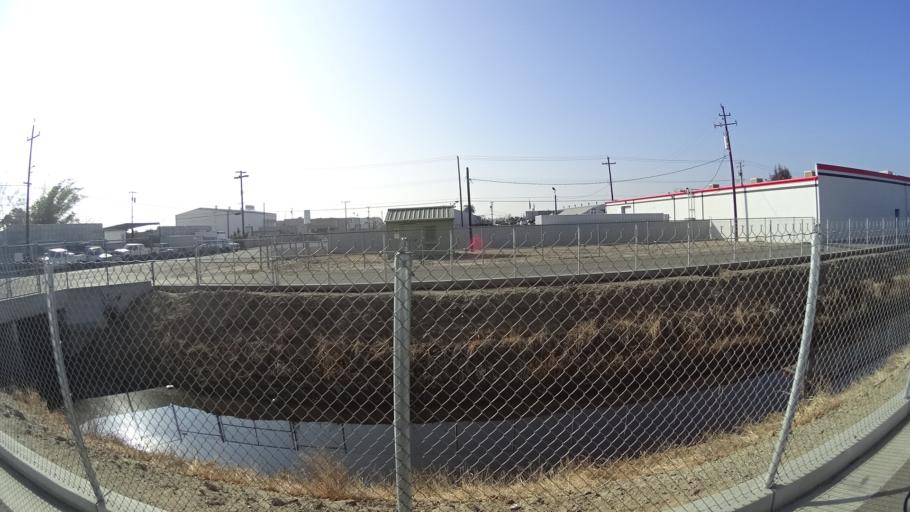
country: US
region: California
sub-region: Kern County
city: Bakersfield
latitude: 35.3819
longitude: -118.9998
